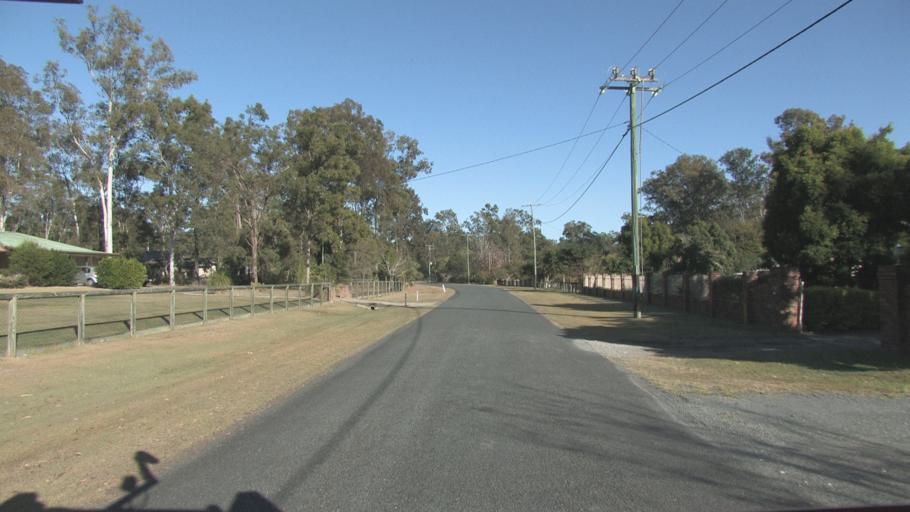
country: AU
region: Queensland
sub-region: Logan
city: North Maclean
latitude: -27.7470
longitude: 153.0127
